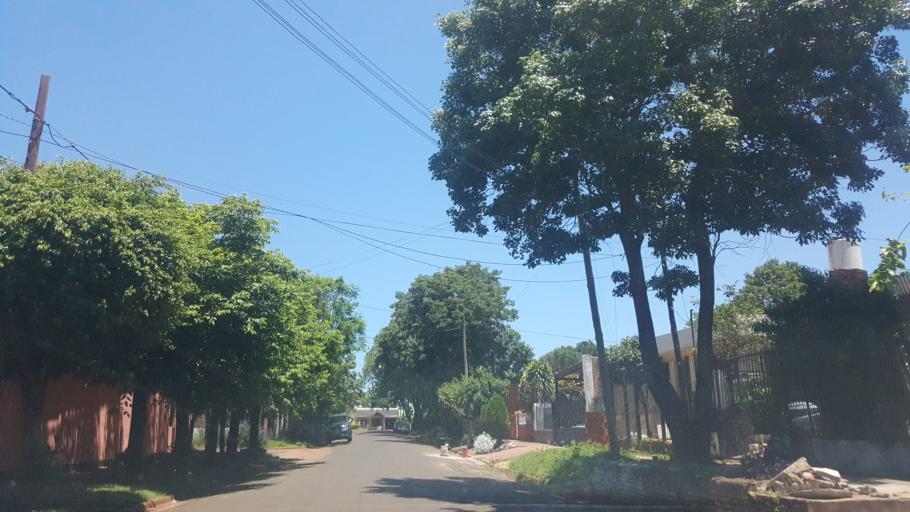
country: AR
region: Misiones
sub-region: Departamento de Capital
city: Posadas
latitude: -27.3859
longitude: -55.9175
